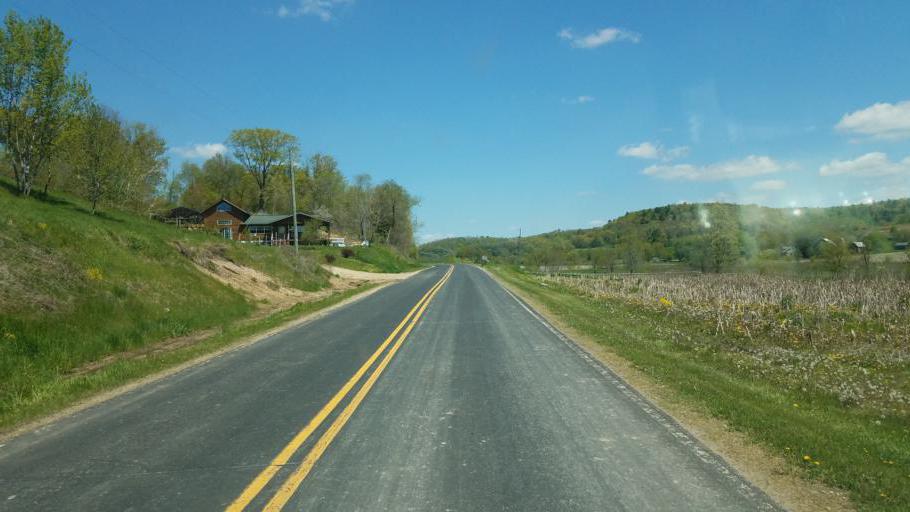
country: US
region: Wisconsin
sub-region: Vernon County
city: Hillsboro
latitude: 43.5771
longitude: -90.4416
